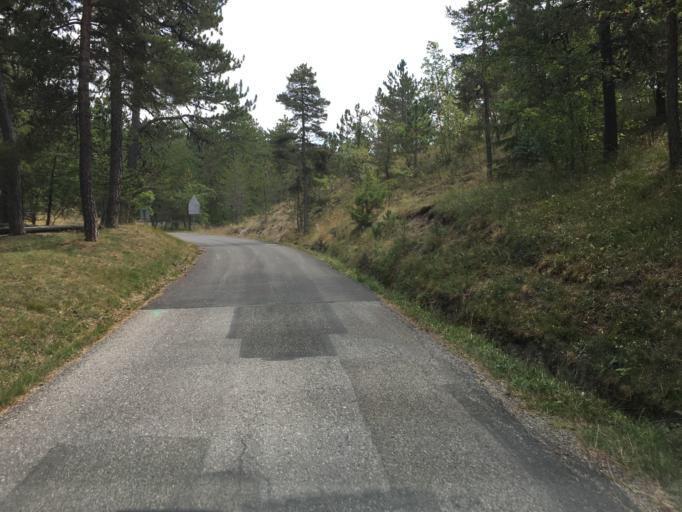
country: FR
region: Provence-Alpes-Cote d'Azur
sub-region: Departement des Alpes-de-Haute-Provence
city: Digne-les-Bains
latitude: 44.2152
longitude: 6.1473
